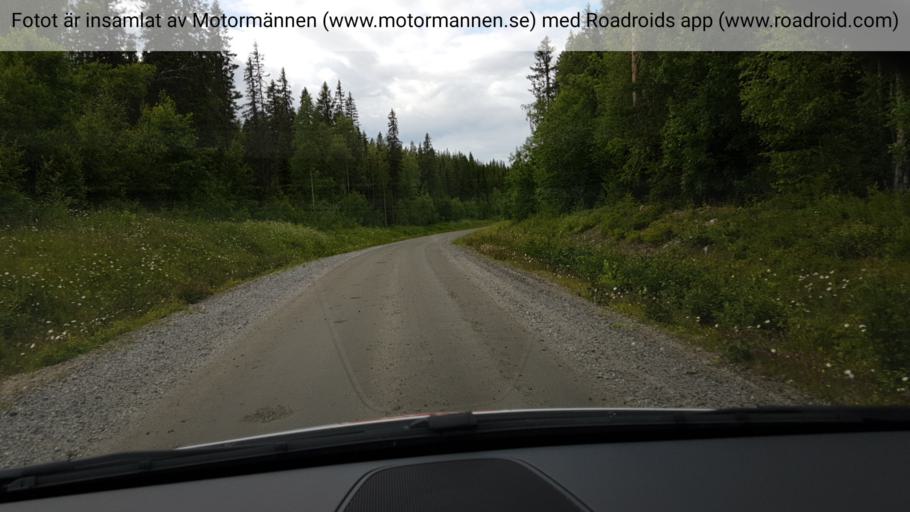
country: SE
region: Vaesterbotten
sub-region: Dorotea Kommun
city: Dorotea
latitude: 63.9222
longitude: 16.1808
